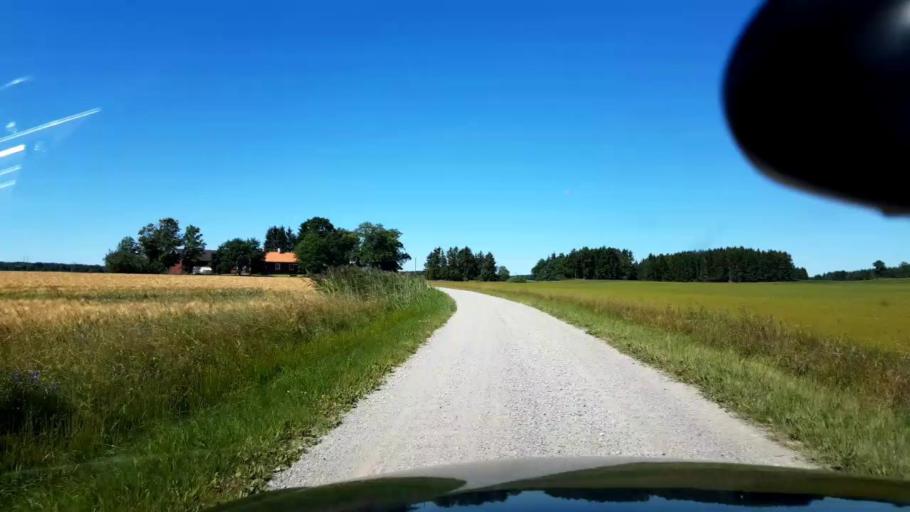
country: SE
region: Stockholm
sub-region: Sigtuna Kommun
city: Sigtuna
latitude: 59.6162
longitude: 17.6393
